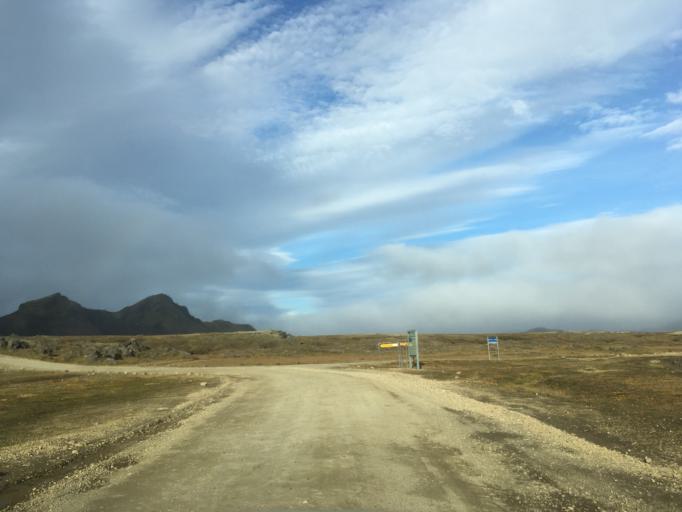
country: IS
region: South
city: Vestmannaeyjar
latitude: 64.0045
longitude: -19.0369
